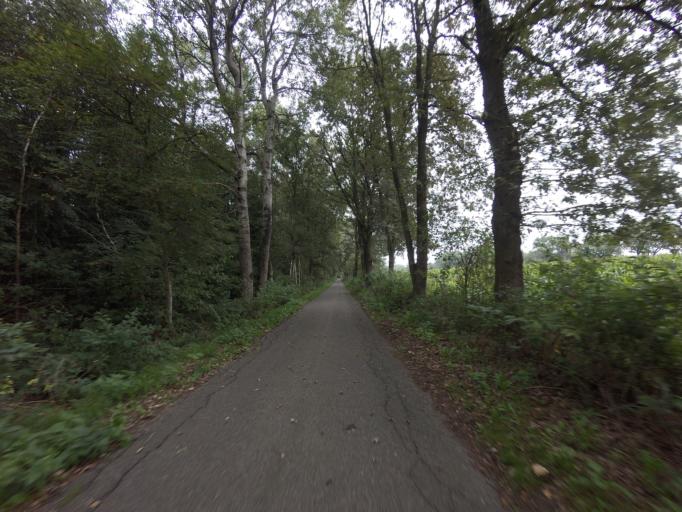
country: NL
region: Drenthe
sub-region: Gemeente Westerveld
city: Dwingeloo
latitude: 52.9053
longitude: 6.4707
